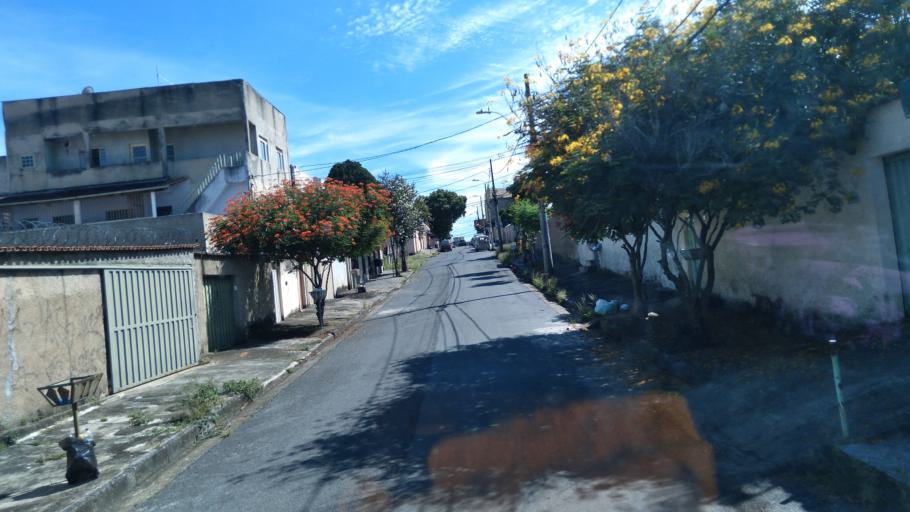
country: BR
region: Minas Gerais
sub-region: Contagem
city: Contagem
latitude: -19.9049
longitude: -44.0043
